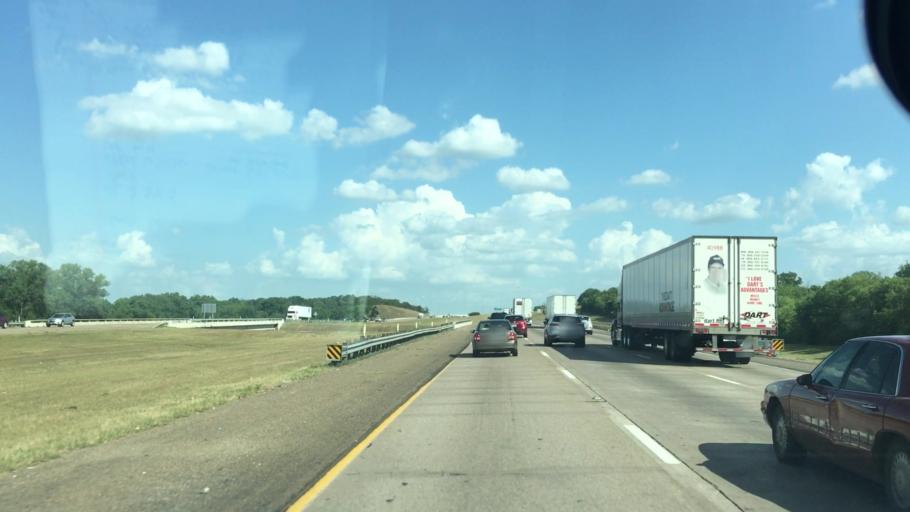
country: US
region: Texas
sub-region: Dallas County
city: Hutchins
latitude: 32.6752
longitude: -96.7389
